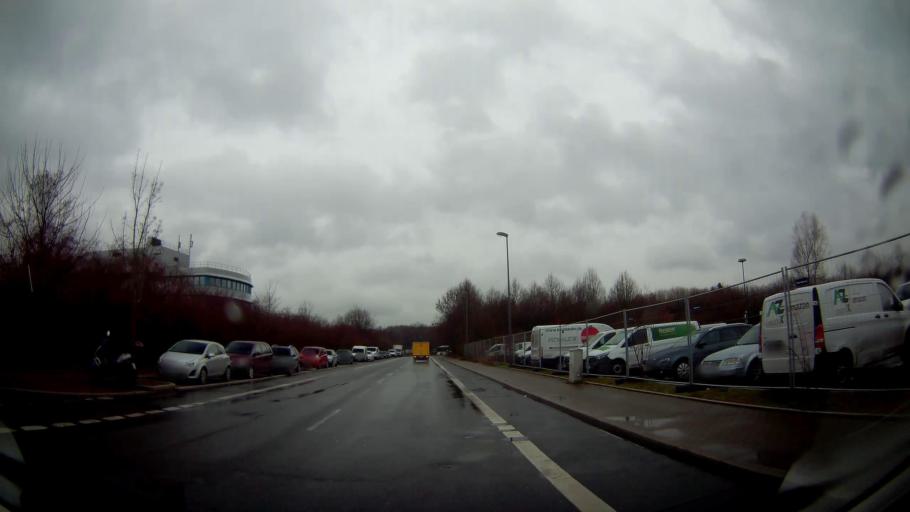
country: DE
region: North Rhine-Westphalia
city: Bochum-Hordel
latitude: 51.5177
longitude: 7.1999
